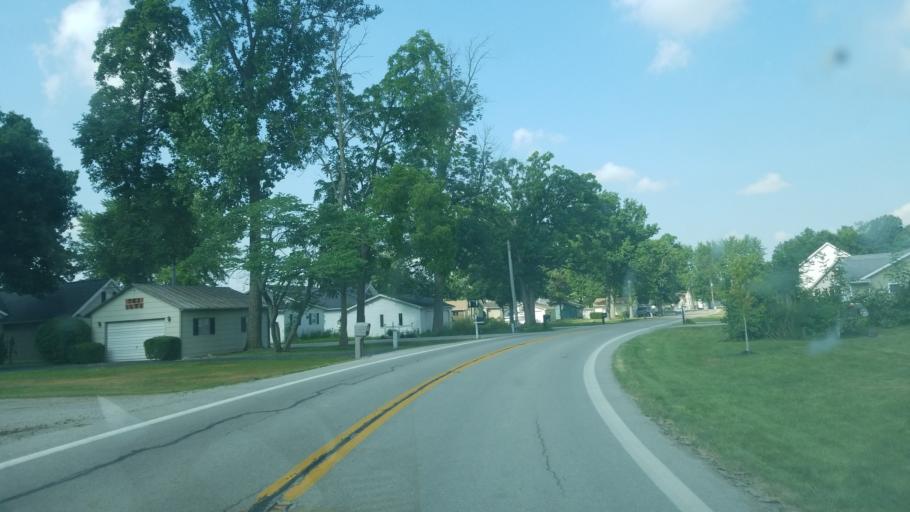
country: US
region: Ohio
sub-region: Logan County
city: Russells Point
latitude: 40.5067
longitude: -83.8469
